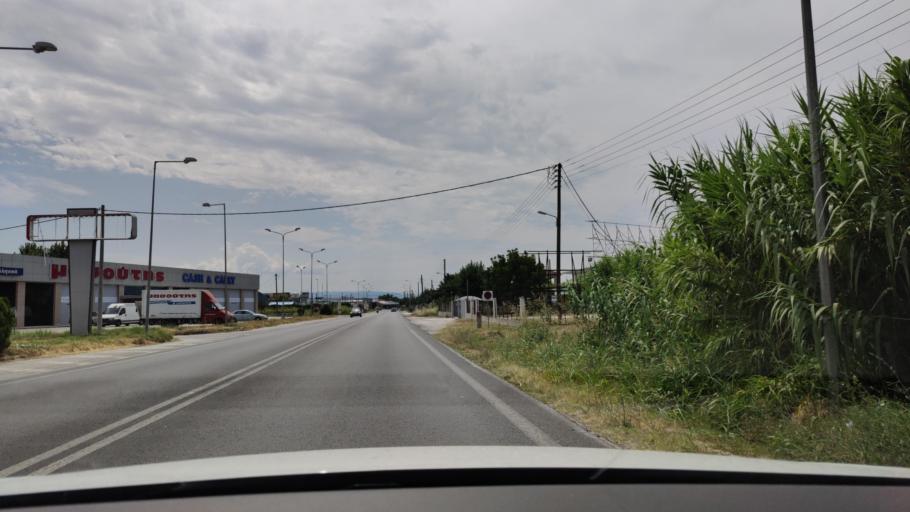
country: GR
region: Central Macedonia
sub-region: Nomos Serron
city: Serres
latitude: 41.0682
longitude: 23.5405
